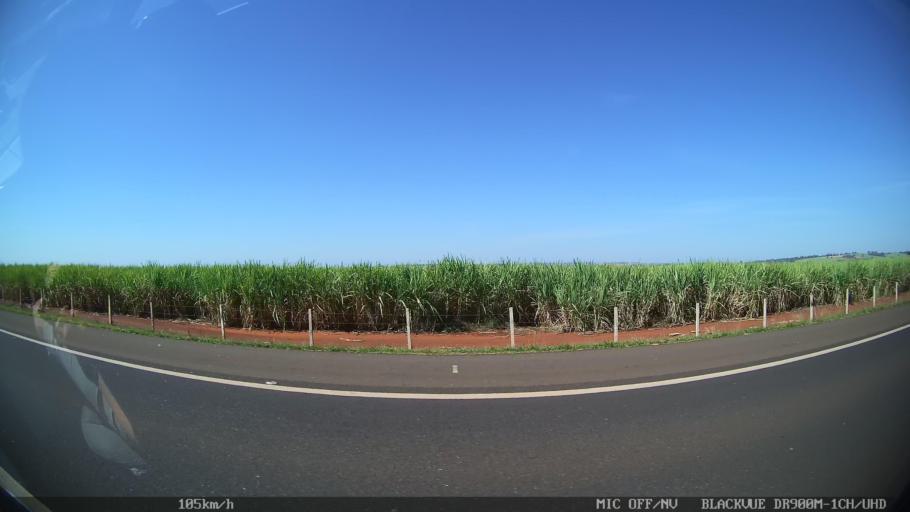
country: BR
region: Sao Paulo
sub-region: Batatais
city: Batatais
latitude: -20.7791
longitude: -47.5485
